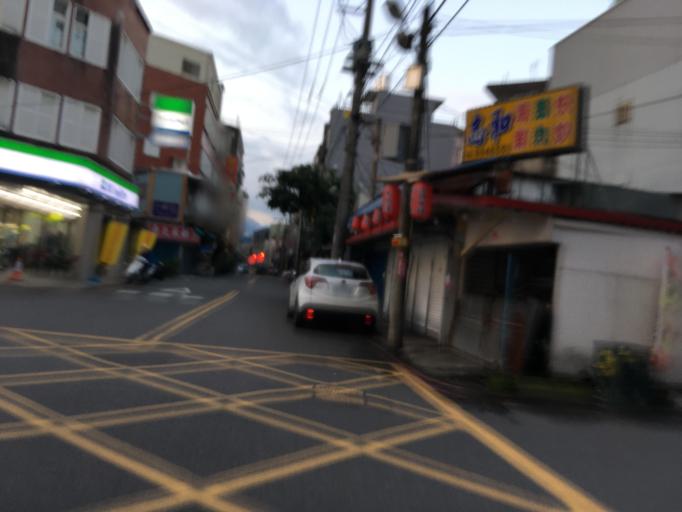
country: TW
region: Taiwan
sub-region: Yilan
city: Yilan
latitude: 24.6743
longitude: 121.7685
